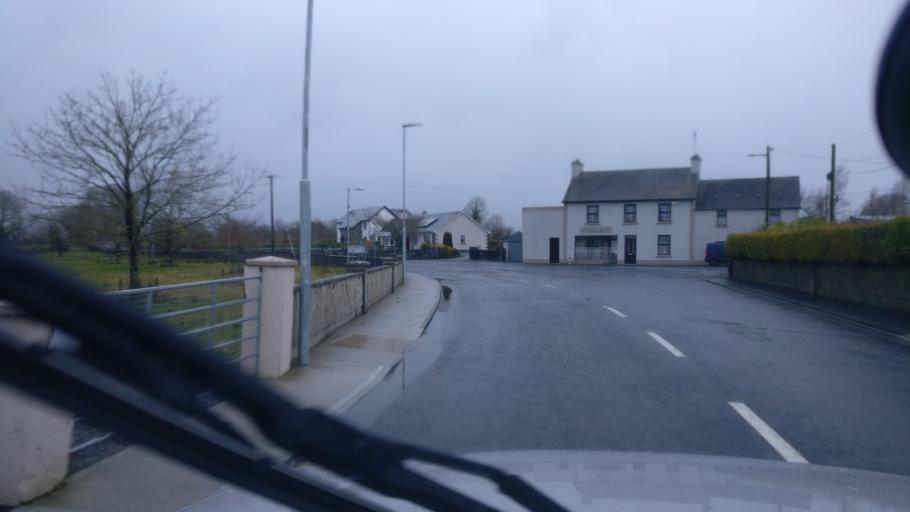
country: IE
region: Connaught
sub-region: County Galway
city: Portumna
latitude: 53.1024
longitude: -8.3936
